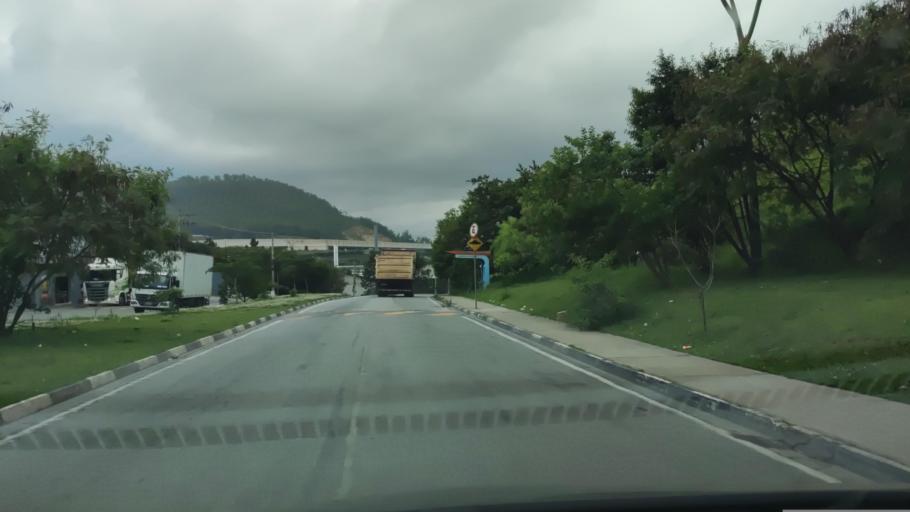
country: BR
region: Sao Paulo
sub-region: Cajamar
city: Cajamar
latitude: -23.3386
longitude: -46.8457
